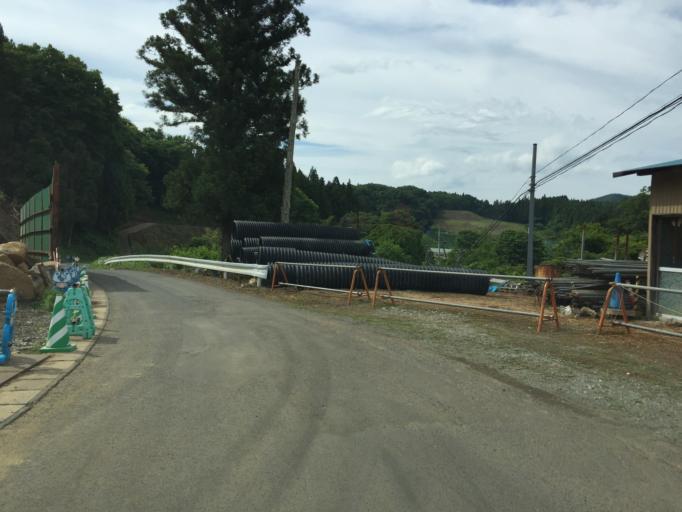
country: JP
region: Fukushima
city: Funehikimachi-funehiki
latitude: 37.5105
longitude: 140.6504
